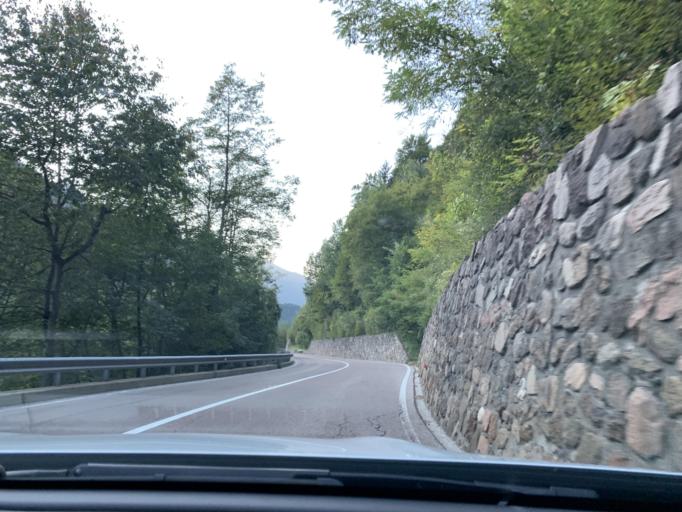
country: IT
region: Trentino-Alto Adige
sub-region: Bolzano
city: Nova Ponente
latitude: 46.4444
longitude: 11.4606
